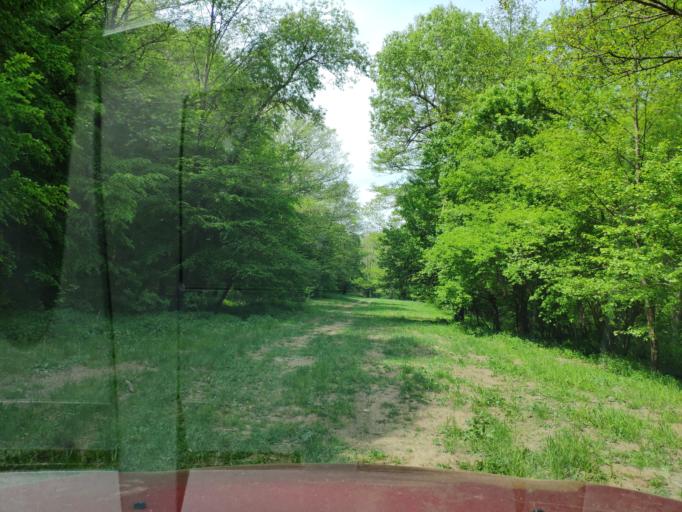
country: SK
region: Banskobystricky
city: Rimavska Sobota
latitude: 48.4858
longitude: 20.0651
